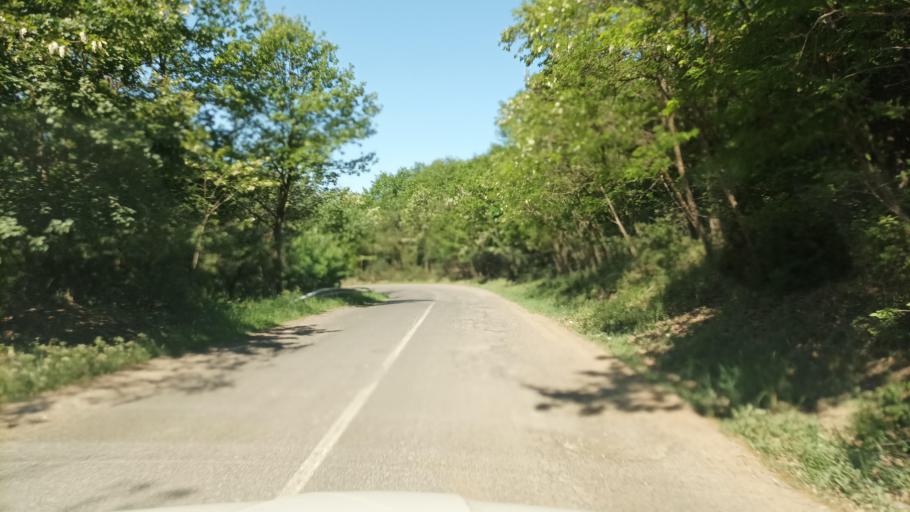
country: HU
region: Pest
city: Acsa
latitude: 47.7901
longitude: 19.4047
